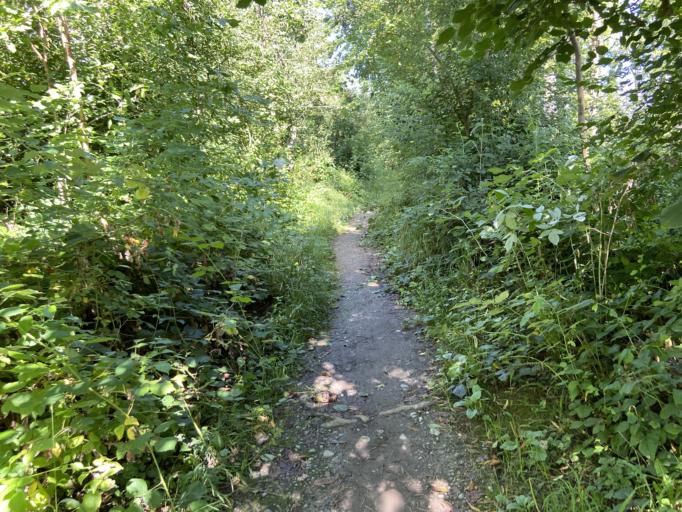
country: CH
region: Zurich
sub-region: Bezirk Meilen
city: Oetwil am See
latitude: 47.2652
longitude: 8.7188
